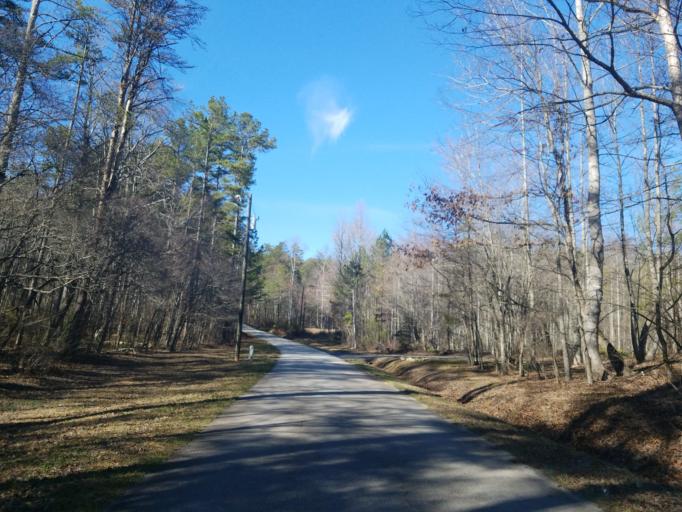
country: US
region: Georgia
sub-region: Dawson County
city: Dawsonville
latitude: 34.5228
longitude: -84.2597
